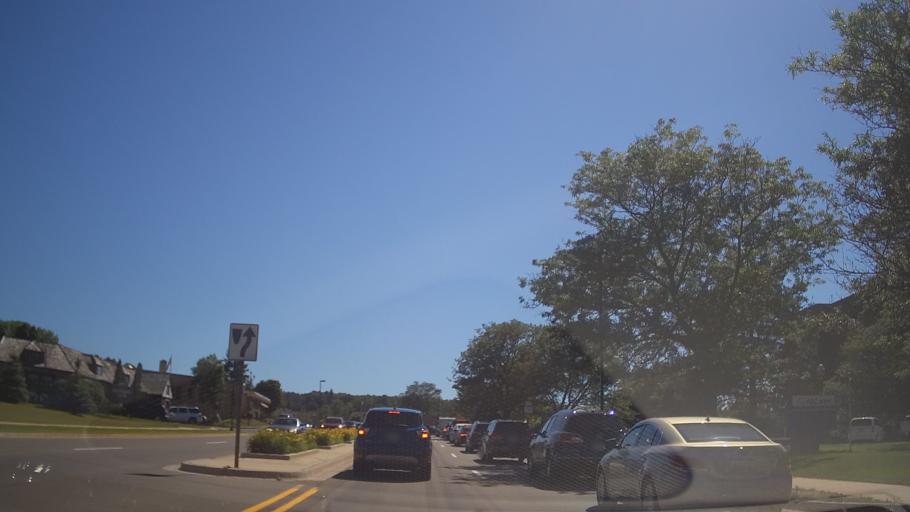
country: US
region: Michigan
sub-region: Emmet County
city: Petoskey
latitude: 45.3726
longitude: -84.9694
